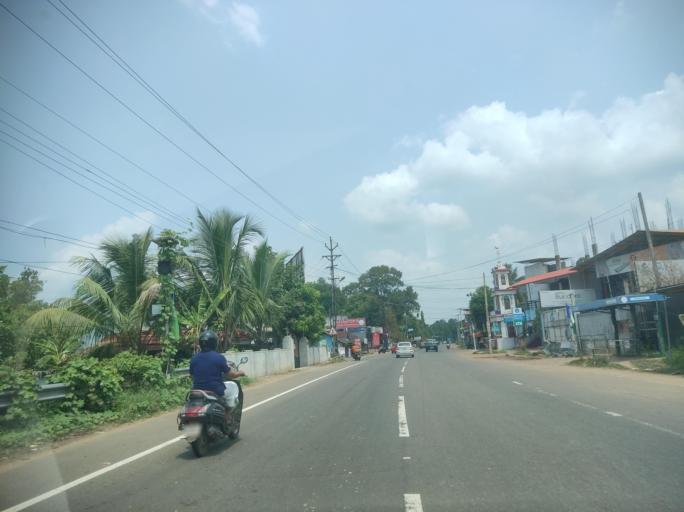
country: IN
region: Kerala
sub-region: Kottayam
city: Changanacheri
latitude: 9.4163
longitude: 76.5502
